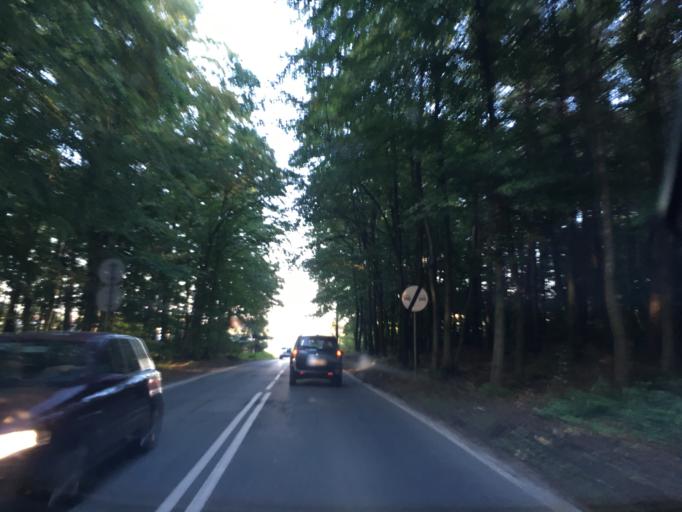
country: PL
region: Pomeranian Voivodeship
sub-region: Gdynia
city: Wielki Kack
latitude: 54.4641
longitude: 18.5088
